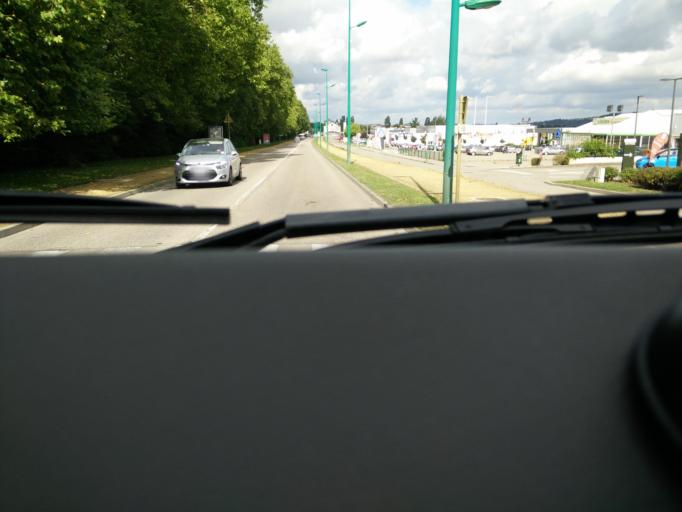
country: FR
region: Lorraine
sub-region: Departement de la Meuse
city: Verdun
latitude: 49.1456
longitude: 5.4072
